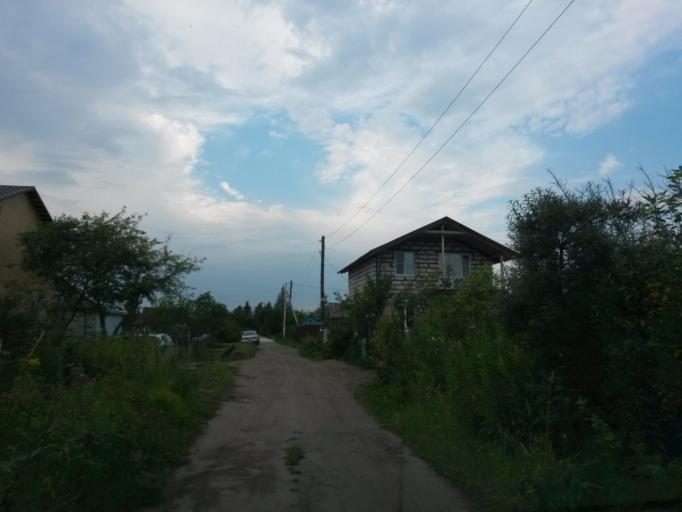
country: RU
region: Jaroslavl
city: Yaroslavl
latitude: 57.6079
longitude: 39.7863
